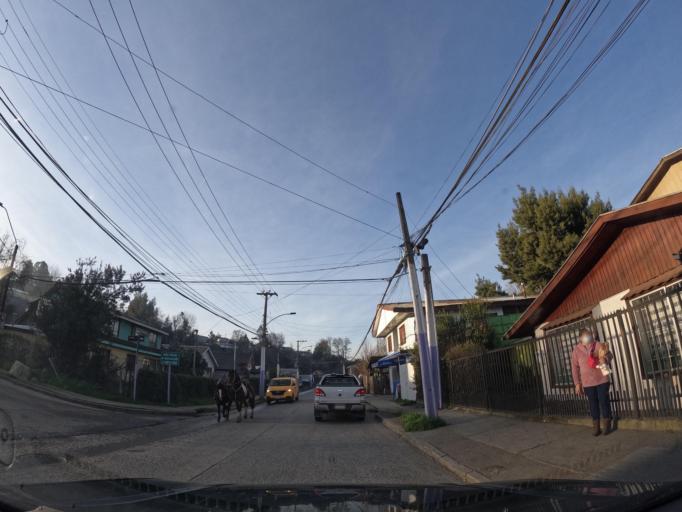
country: CL
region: Biobio
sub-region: Provincia de Concepcion
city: Concepcion
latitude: -36.8396
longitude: -73.0066
